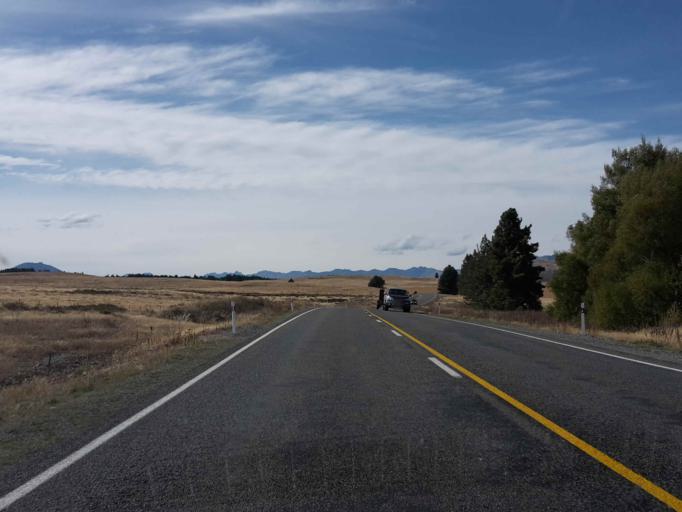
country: NZ
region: Canterbury
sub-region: Timaru District
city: Pleasant Point
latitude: -44.0281
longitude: 170.3966
